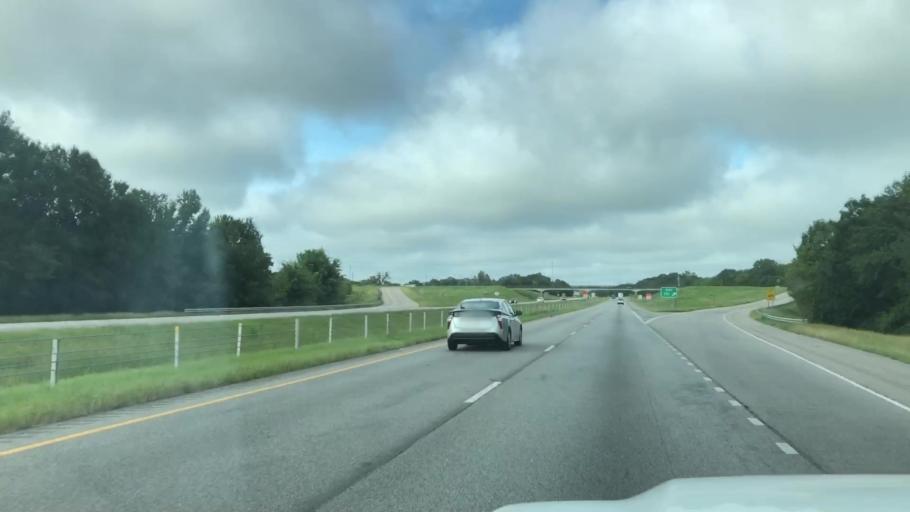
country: US
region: Alabama
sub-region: Lowndes County
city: Hayneville
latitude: 32.1128
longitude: -86.4588
